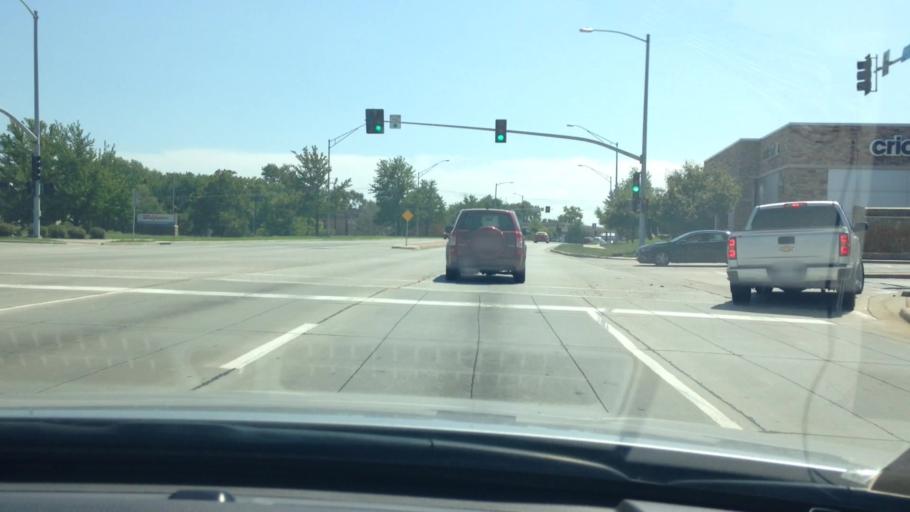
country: US
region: Kansas
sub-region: Johnson County
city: Roeland Park
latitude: 39.0396
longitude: -94.6402
